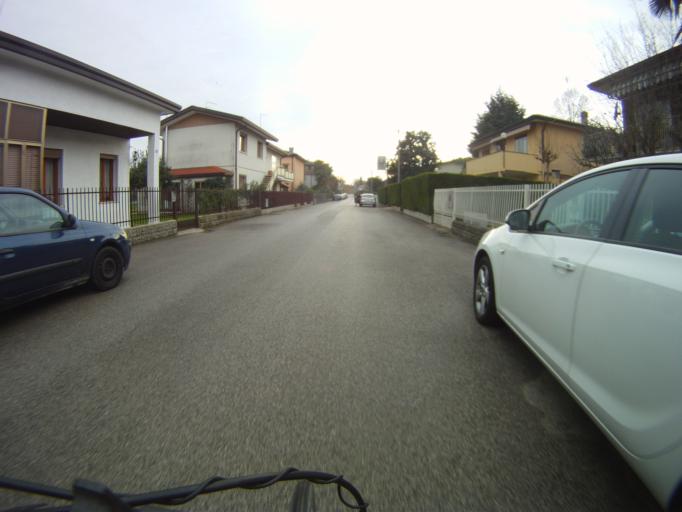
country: IT
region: Veneto
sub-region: Provincia di Padova
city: Ponte San Nicolo
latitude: 45.3817
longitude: 11.9040
